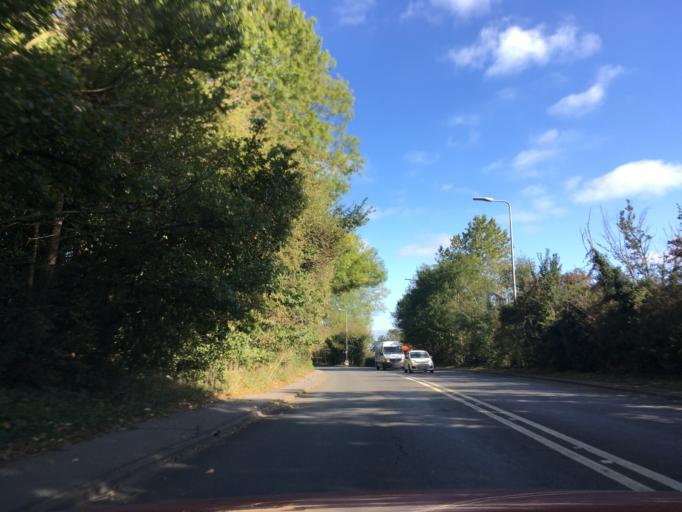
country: GB
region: England
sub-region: Hampshire
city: Tadley
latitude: 51.3958
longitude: -1.1637
